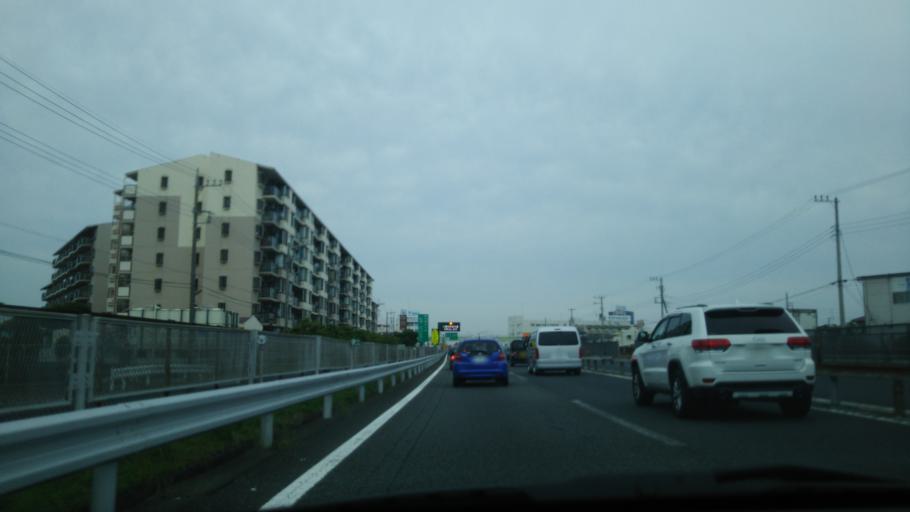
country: JP
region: Kanagawa
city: Atsugi
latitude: 35.4113
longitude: 139.3467
